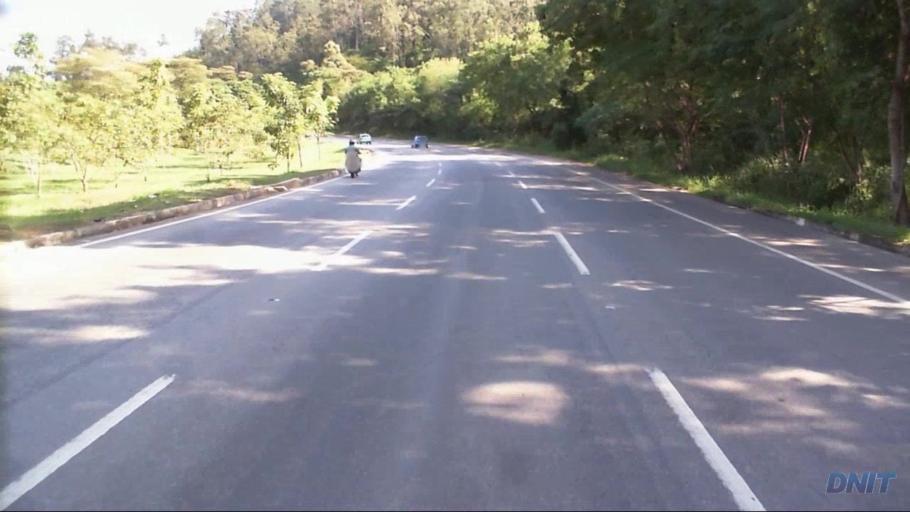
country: BR
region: Minas Gerais
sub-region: Coronel Fabriciano
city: Coronel Fabriciano
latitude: -19.5120
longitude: -42.5754
